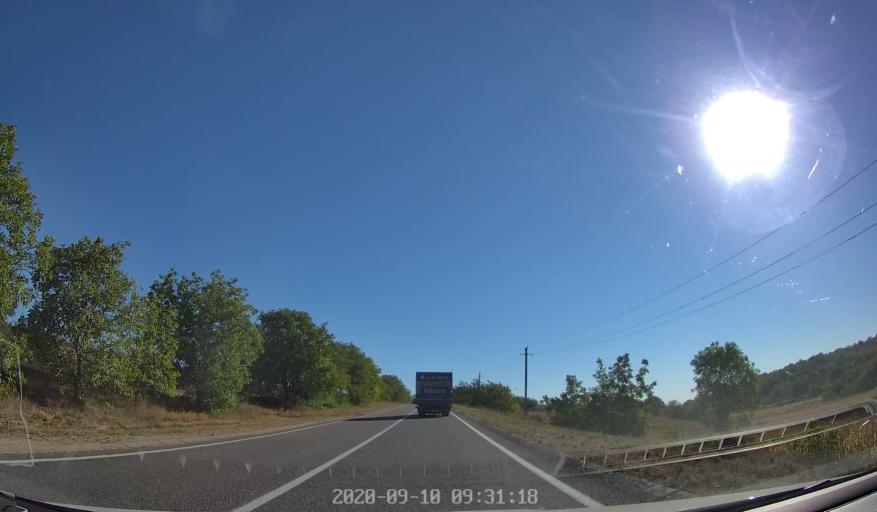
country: MD
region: Soldanesti
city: Soldanesti
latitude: 47.7032
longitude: 28.8396
